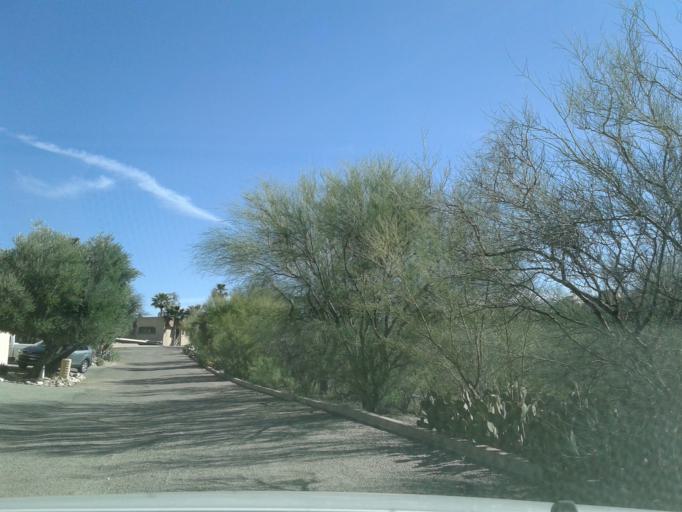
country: US
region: Arizona
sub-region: Pima County
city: Catalina Foothills
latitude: 32.3116
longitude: -110.8907
